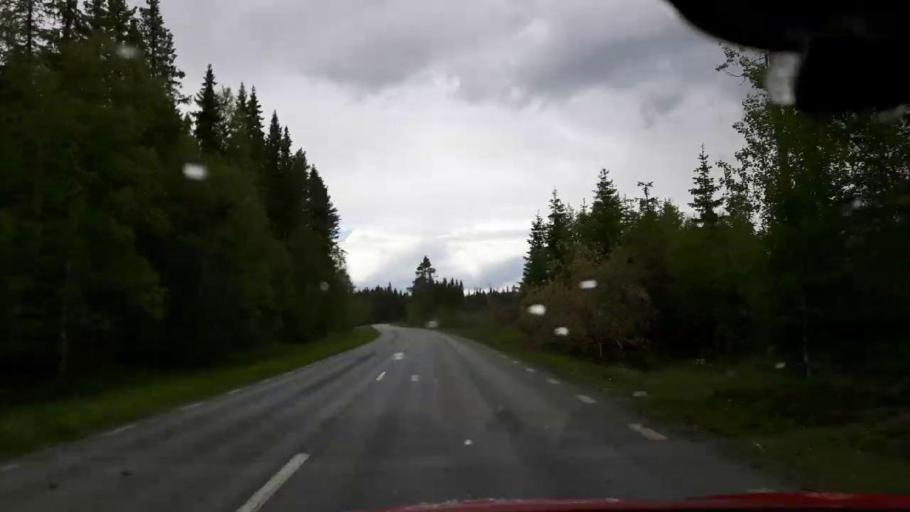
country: SE
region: Jaemtland
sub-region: Krokoms Kommun
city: Krokom
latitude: 63.4193
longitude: 14.2269
